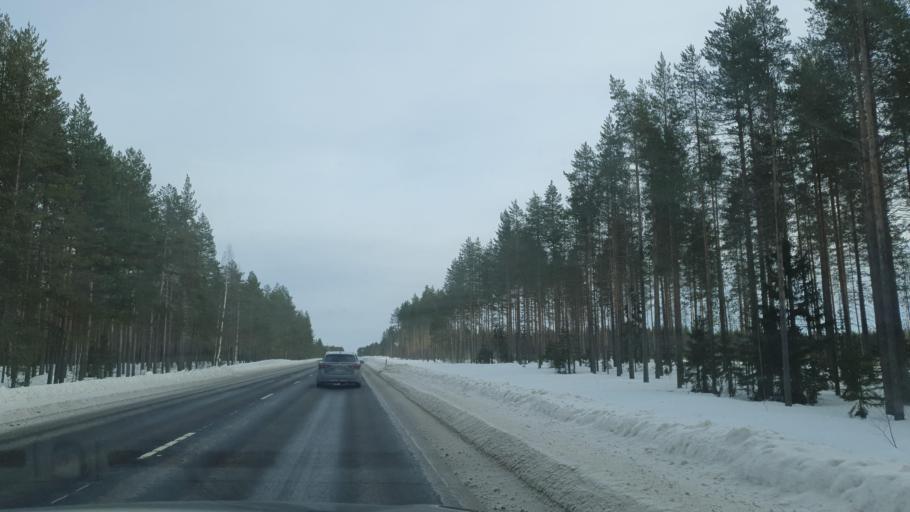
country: FI
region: Kainuu
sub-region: Kajaani
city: Vaala
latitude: 64.5549
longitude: 27.0404
